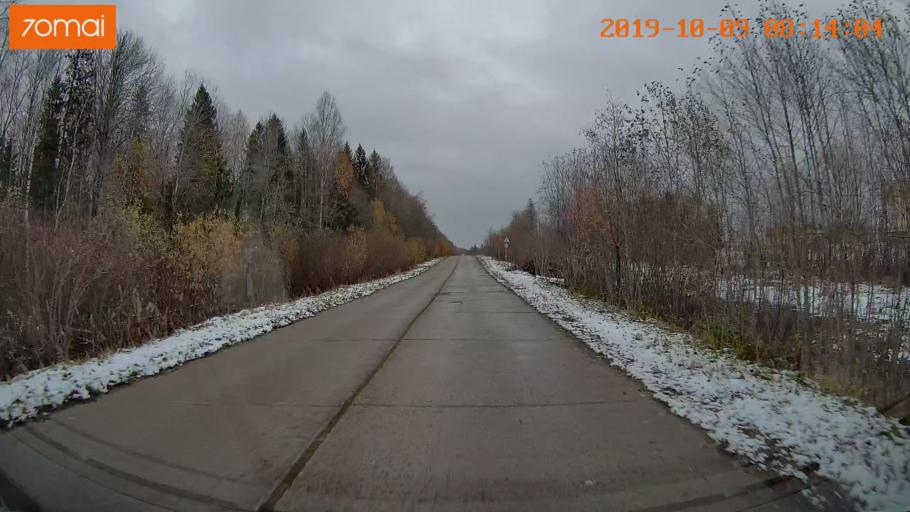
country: RU
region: Vologda
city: Gryazovets
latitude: 58.7267
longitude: 40.1498
